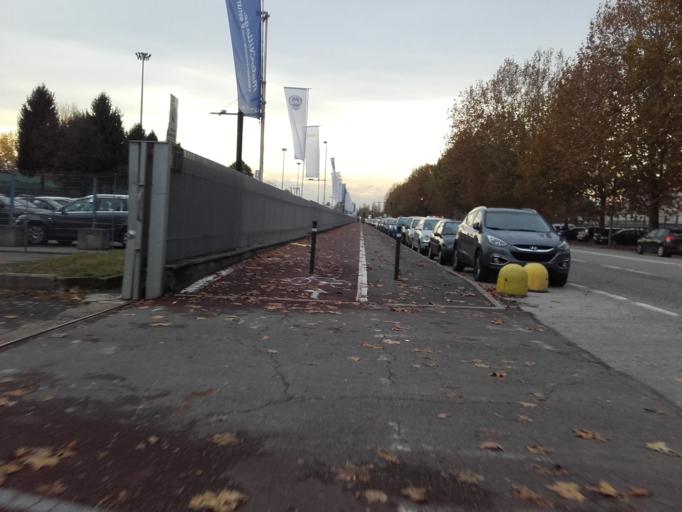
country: IT
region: Piedmont
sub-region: Provincia di Torino
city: Turin
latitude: 45.1096
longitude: 7.7119
